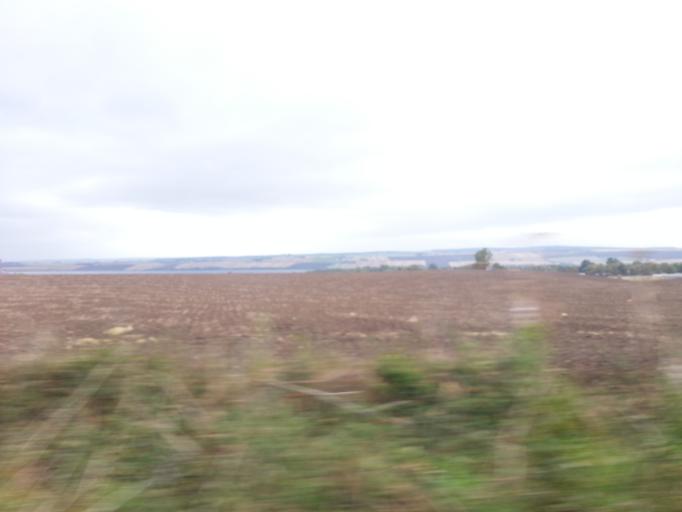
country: GB
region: Scotland
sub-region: Highland
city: Evanton
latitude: 57.6701
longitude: -4.3233
